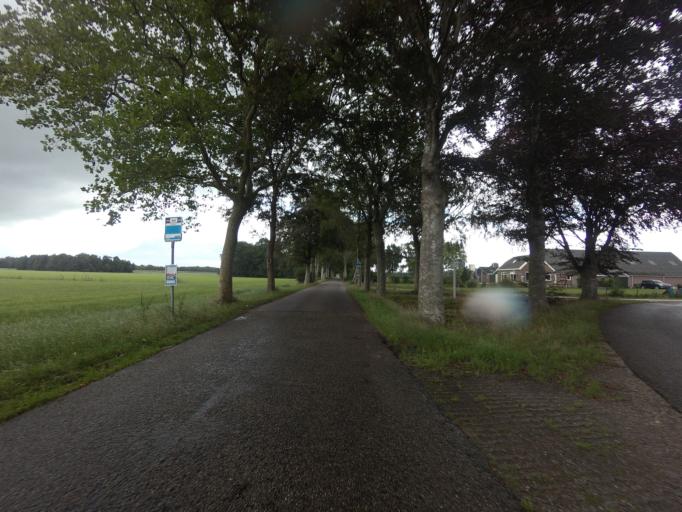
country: NL
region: Friesland
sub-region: Gemeente Weststellingwerf
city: Noordwolde
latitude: 52.9641
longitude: 6.2436
